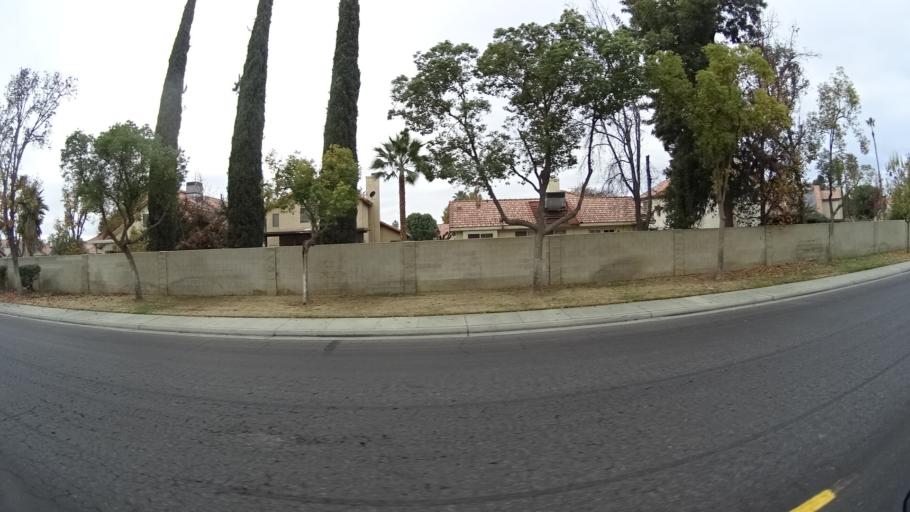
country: US
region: California
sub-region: Kern County
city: Greenacres
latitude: 35.3010
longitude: -119.0887
